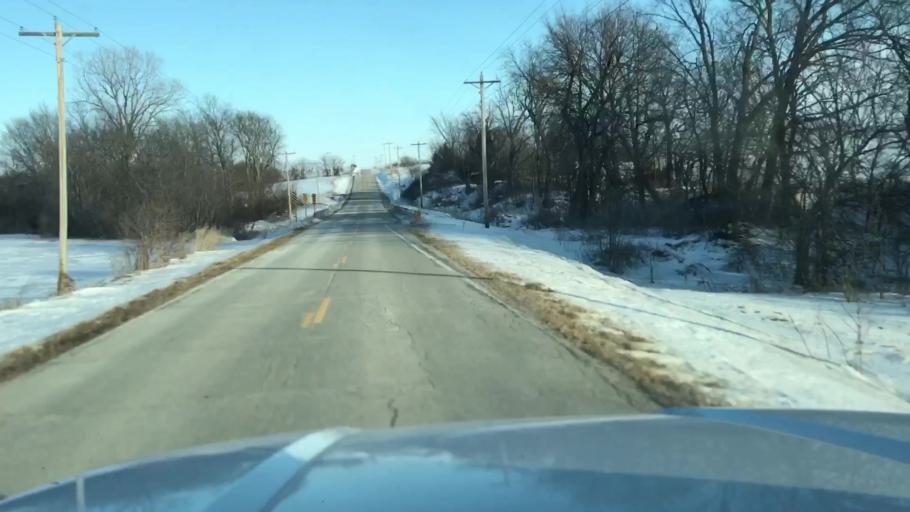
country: US
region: Missouri
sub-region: Andrew County
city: Savannah
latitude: 40.0246
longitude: -94.9048
